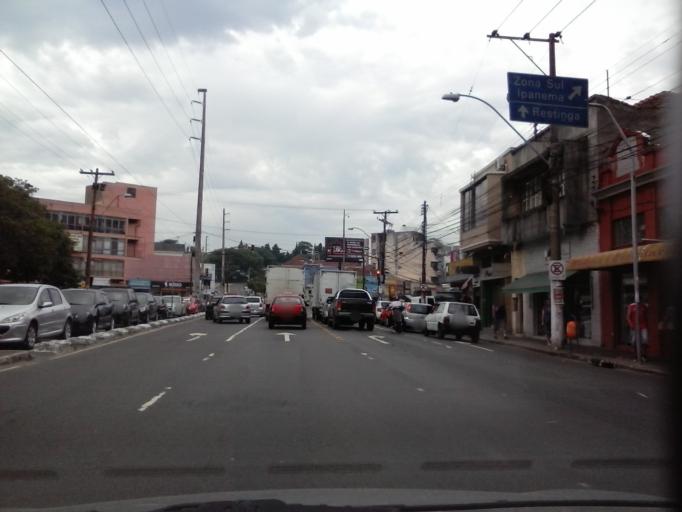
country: BR
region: Rio Grande do Sul
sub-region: Porto Alegre
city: Porto Alegre
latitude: -30.0503
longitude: -51.2131
